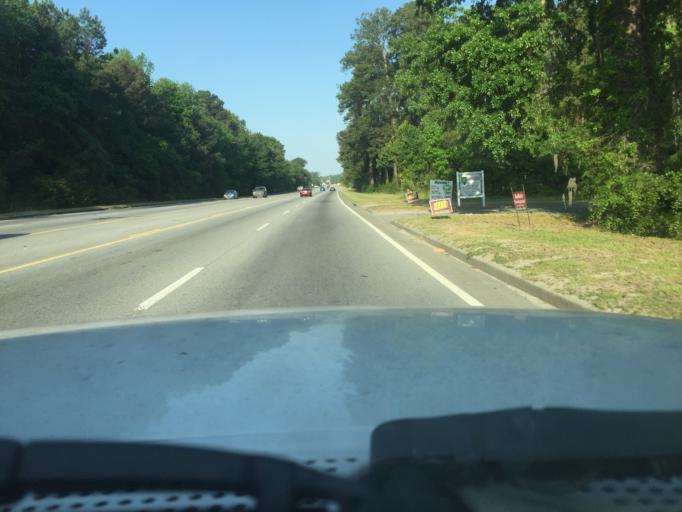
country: US
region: Georgia
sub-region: Chatham County
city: Georgetown
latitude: 32.0409
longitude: -81.1968
